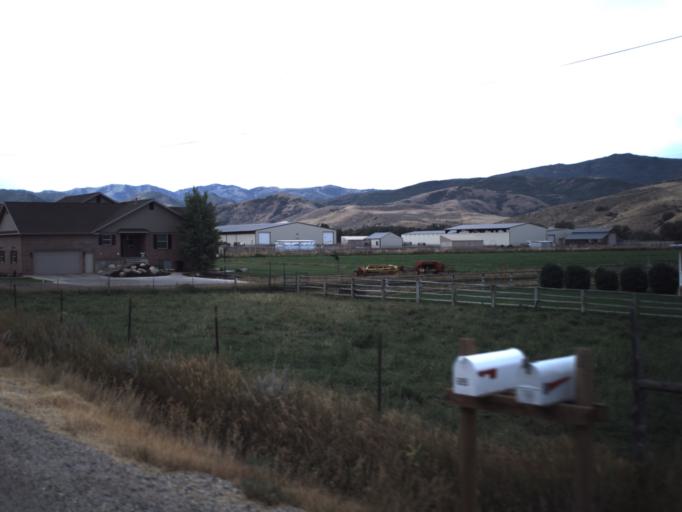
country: US
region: Utah
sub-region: Morgan County
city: Morgan
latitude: 41.0239
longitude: -111.6752
